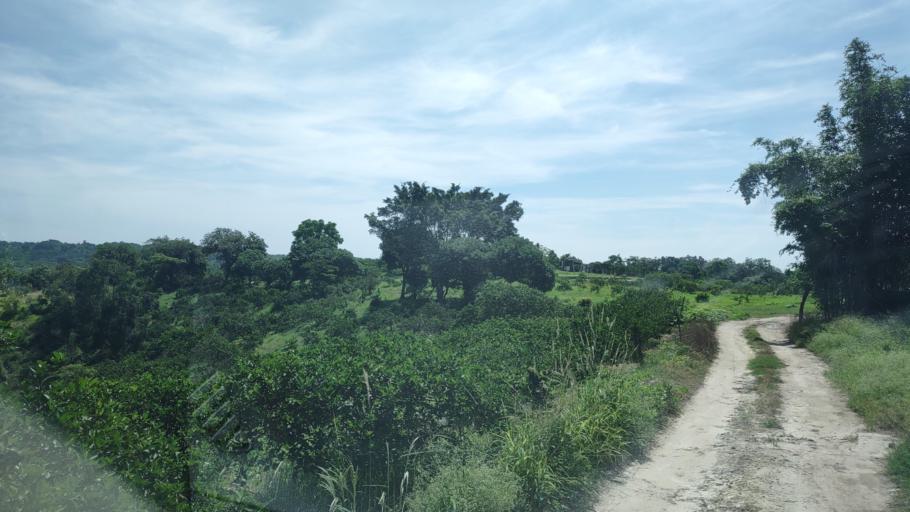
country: MX
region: Veracruz
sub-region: Emiliano Zapata
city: Dos Rios
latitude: 19.4292
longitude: -96.7933
